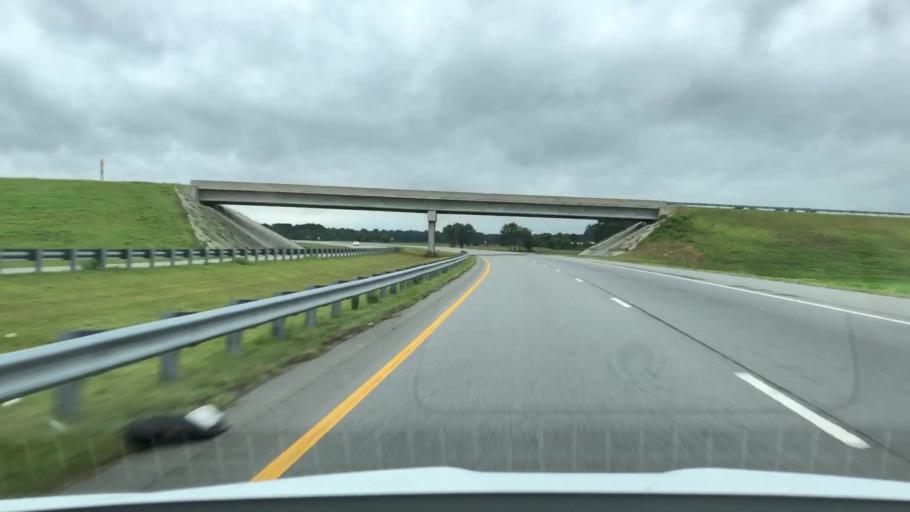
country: US
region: North Carolina
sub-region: Lenoir County
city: Kinston
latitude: 35.2656
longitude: -77.6748
